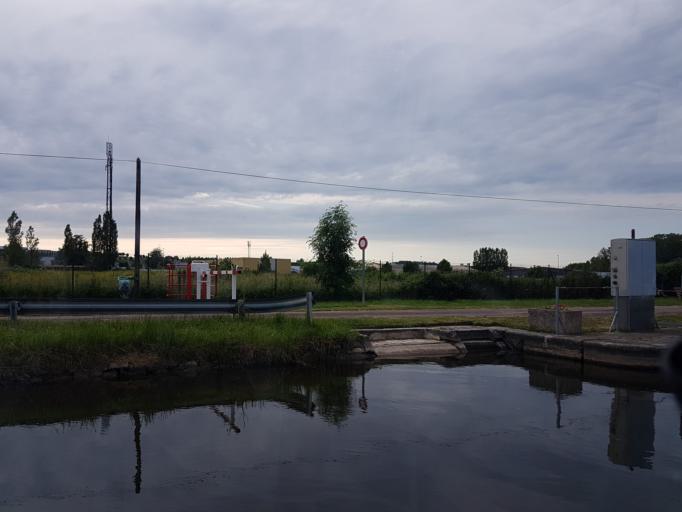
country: FR
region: Bourgogne
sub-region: Departement de l'Yonne
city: Auxerre
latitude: 47.8147
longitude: 3.5802
